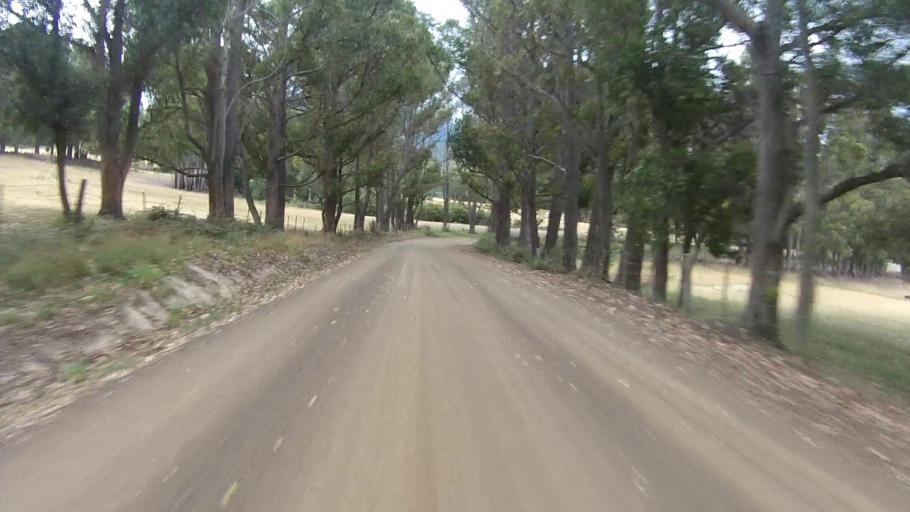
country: AU
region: Tasmania
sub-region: Huon Valley
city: Huonville
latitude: -42.9639
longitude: 147.0771
